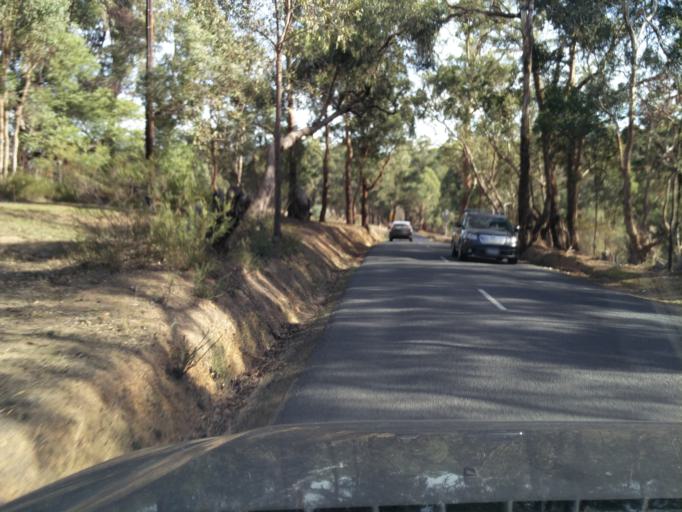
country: AU
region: Victoria
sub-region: Nillumbik
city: Eltham
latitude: -37.7239
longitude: 145.1722
